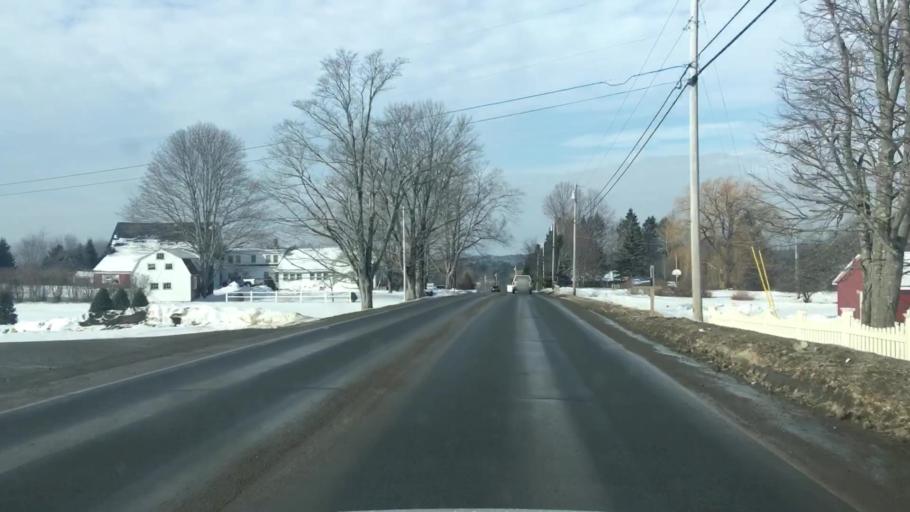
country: US
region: Maine
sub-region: Penobscot County
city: Hermon
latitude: 44.8470
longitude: -68.8715
